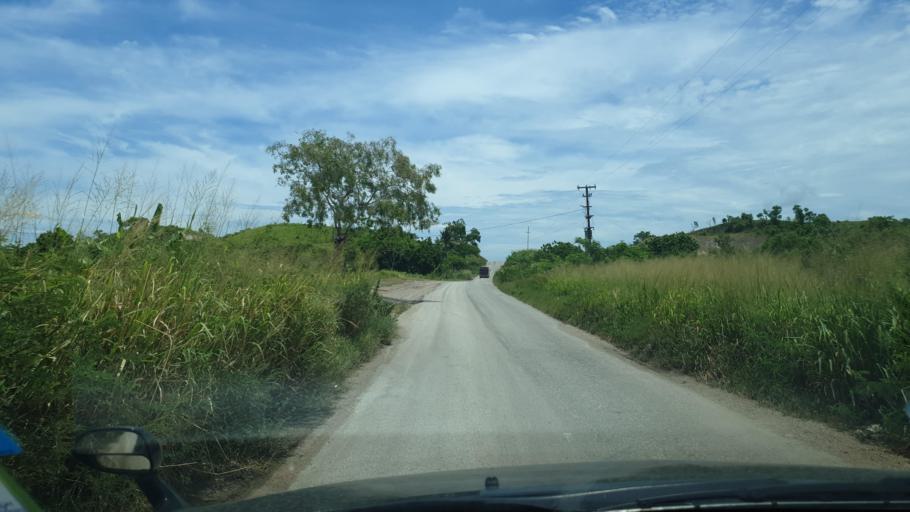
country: PG
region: National Capital
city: Port Moresby
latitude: -9.4275
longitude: 147.0523
